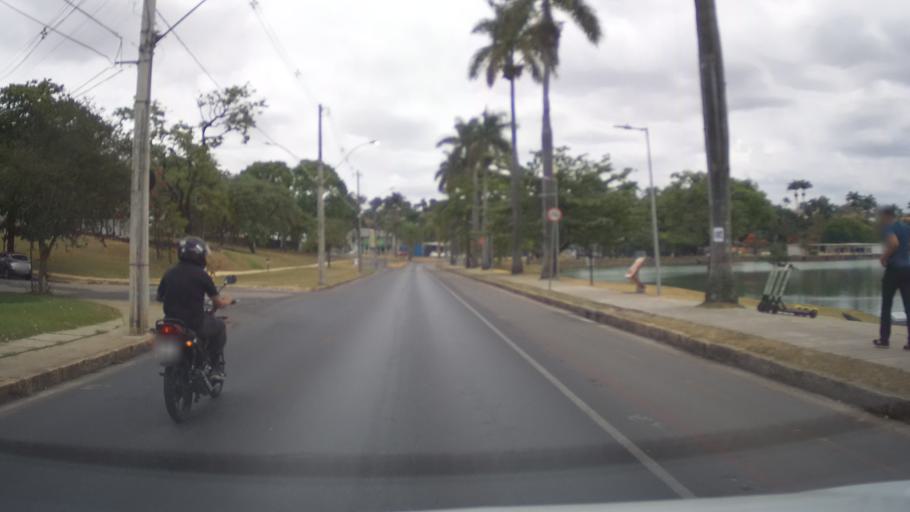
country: BR
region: Minas Gerais
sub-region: Belo Horizonte
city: Belo Horizonte
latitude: -19.8526
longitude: -43.9681
